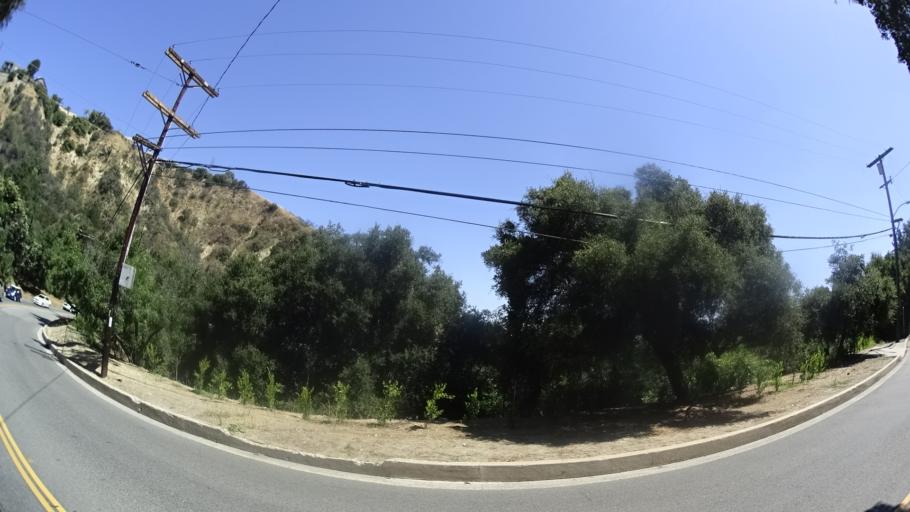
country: US
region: California
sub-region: Los Angeles County
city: Sherman Oaks
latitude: 34.1350
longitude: -118.4528
